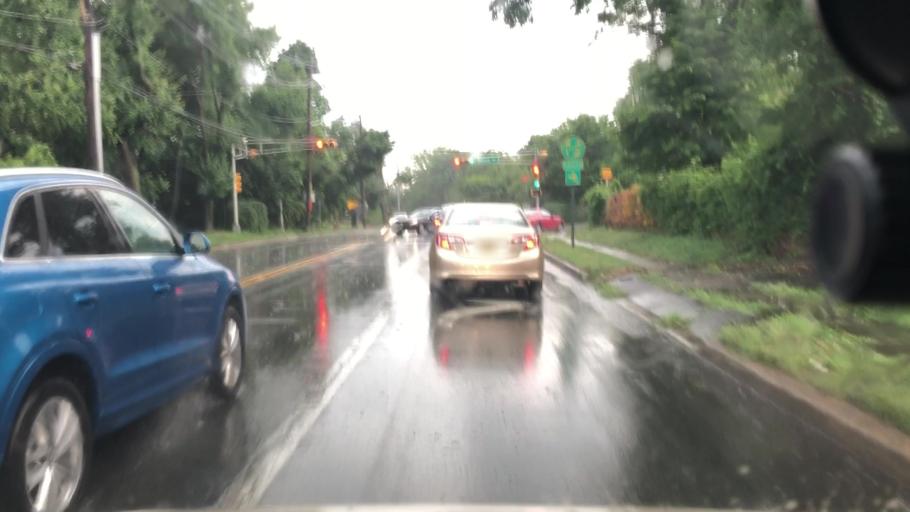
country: US
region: New Jersey
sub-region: Union County
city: Union
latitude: 40.6979
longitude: -74.2575
